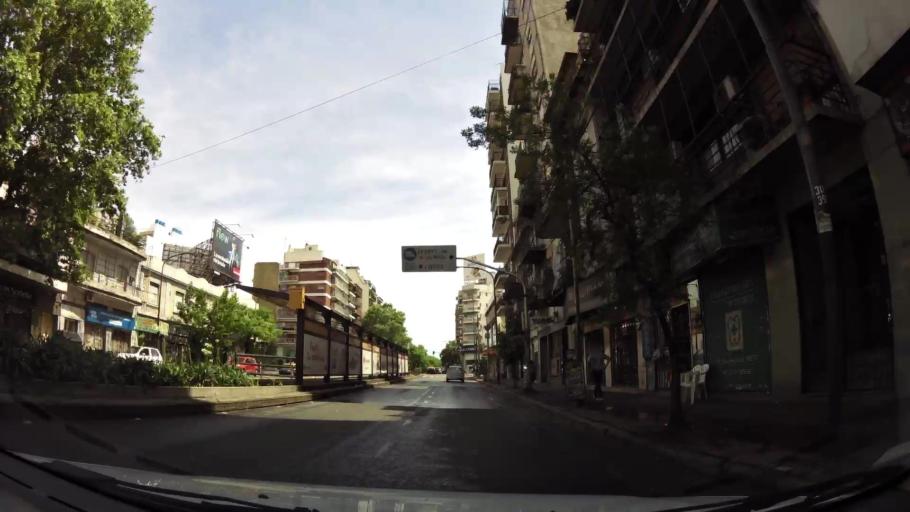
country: AR
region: Buenos Aires F.D.
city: Villa Santa Rita
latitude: -34.6040
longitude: -58.4579
